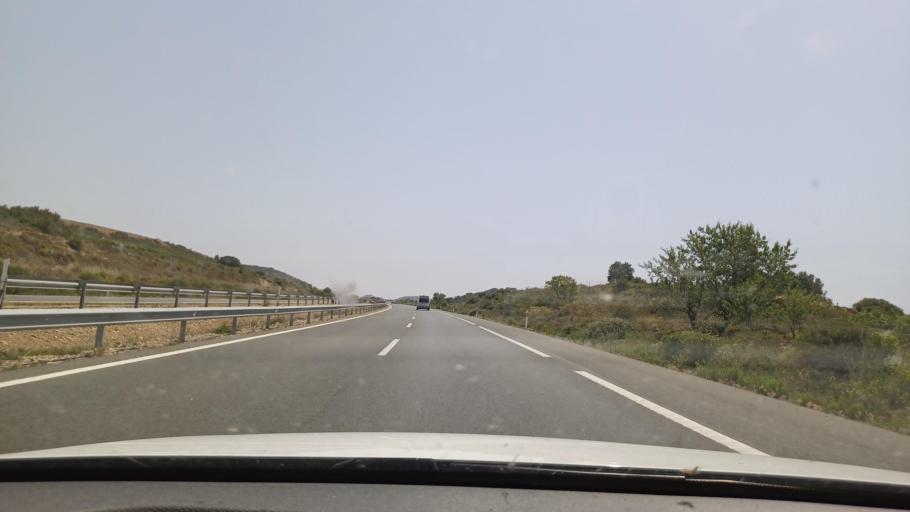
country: ES
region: La Rioja
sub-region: Provincia de La Rioja
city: Navarrete
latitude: 42.4306
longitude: -2.5424
